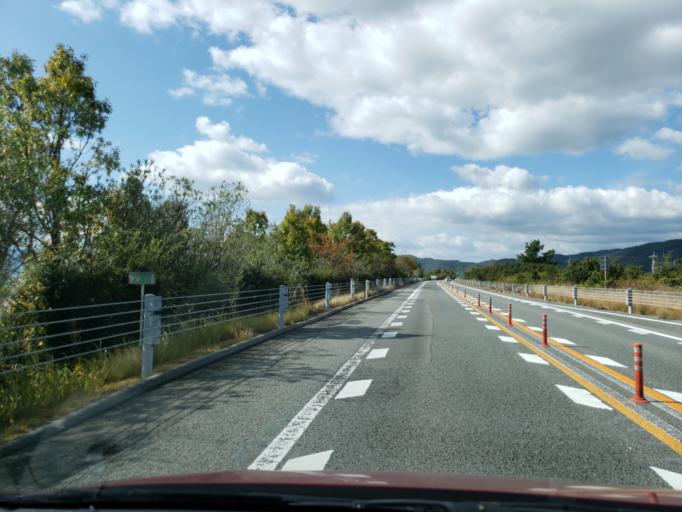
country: JP
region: Tokushima
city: Kamojimacho-jogejima
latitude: 34.1189
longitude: 134.3431
